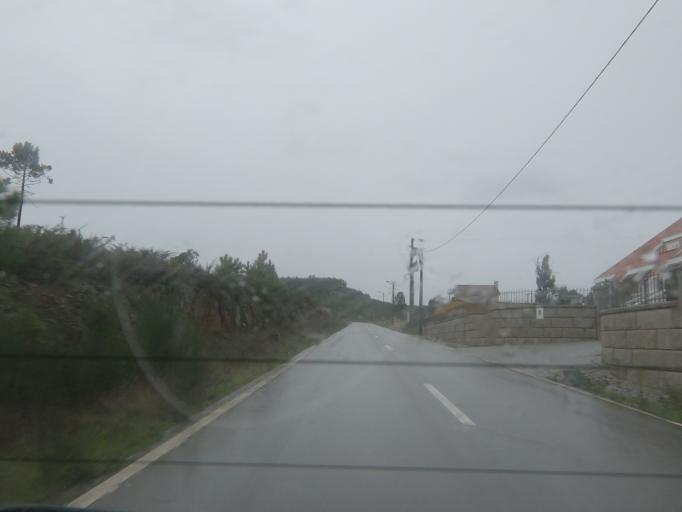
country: PT
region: Vila Real
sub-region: Sabrosa
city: Vilela
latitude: 41.2037
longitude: -7.6809
